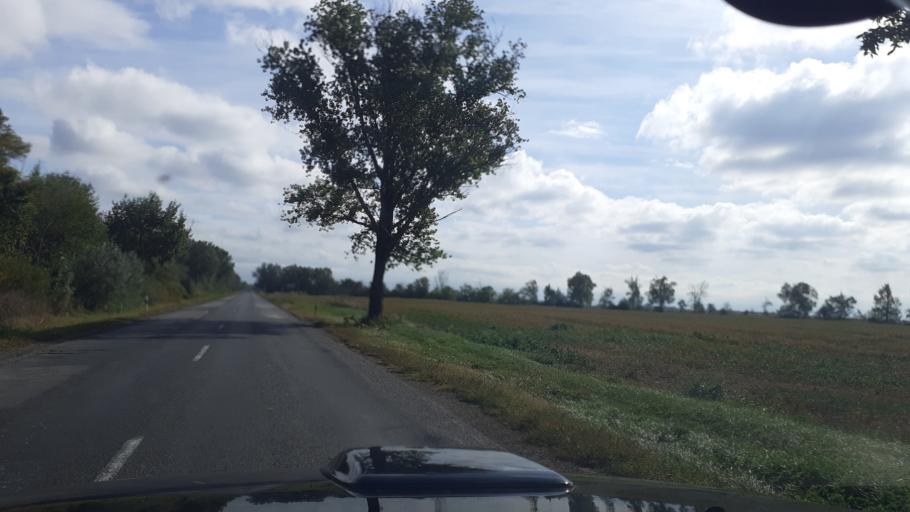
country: HU
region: Bacs-Kiskun
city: Solt
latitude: 46.7981
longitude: 19.0927
